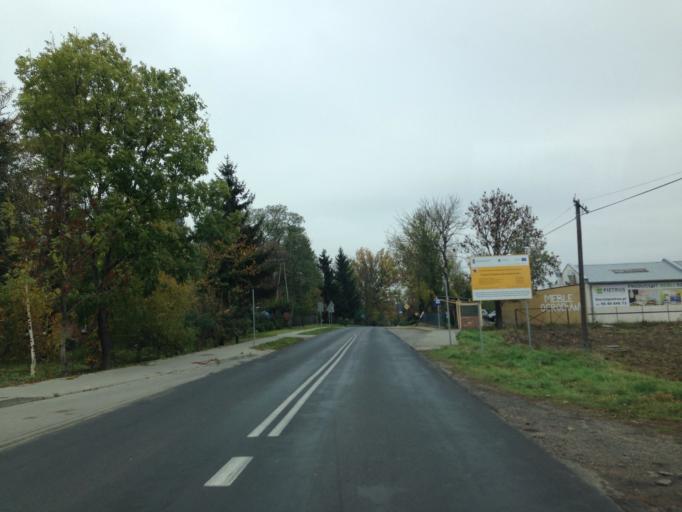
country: PL
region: Kujawsko-Pomorskie
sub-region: Powiat brodnicki
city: Bobrowo
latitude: 53.2858
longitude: 19.3073
